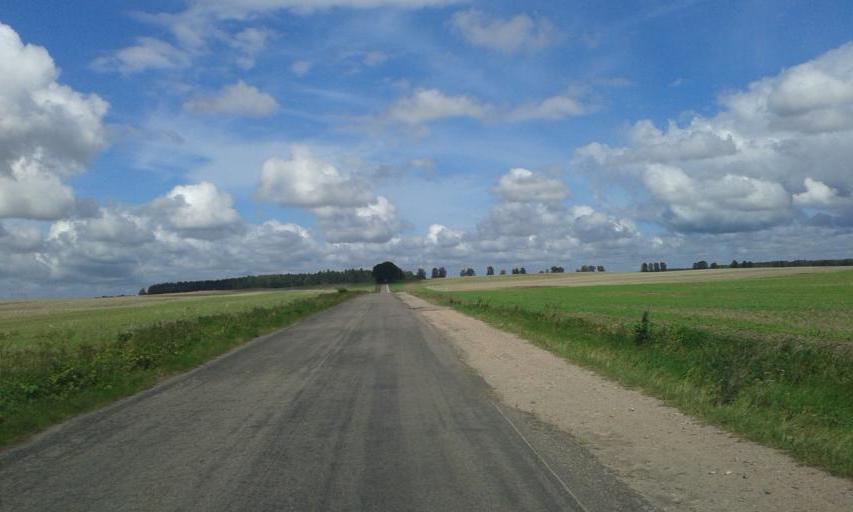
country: PL
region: West Pomeranian Voivodeship
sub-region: Powiat slawienski
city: Slawno
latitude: 54.2871
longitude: 16.6590
